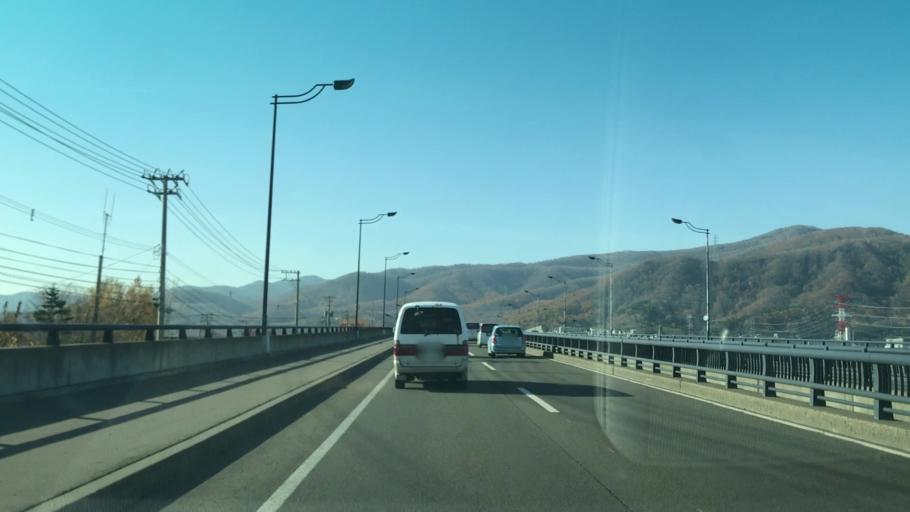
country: JP
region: Hokkaido
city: Sapporo
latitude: 43.1046
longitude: 141.2730
